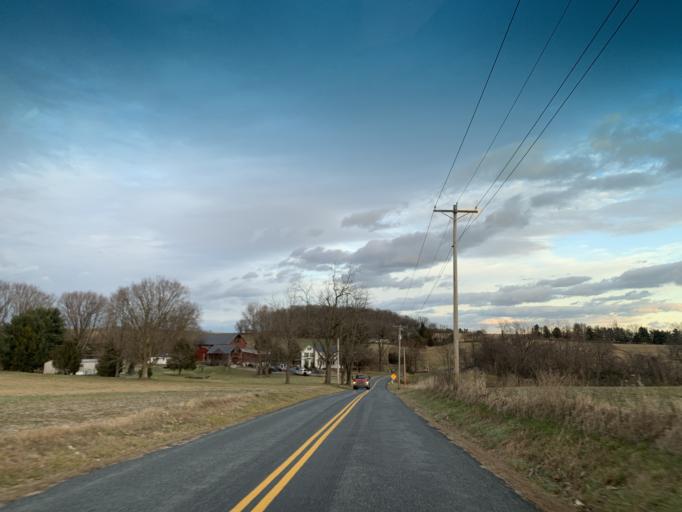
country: US
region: Maryland
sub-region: Harford County
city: Bel Air North
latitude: 39.6492
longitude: -76.3515
